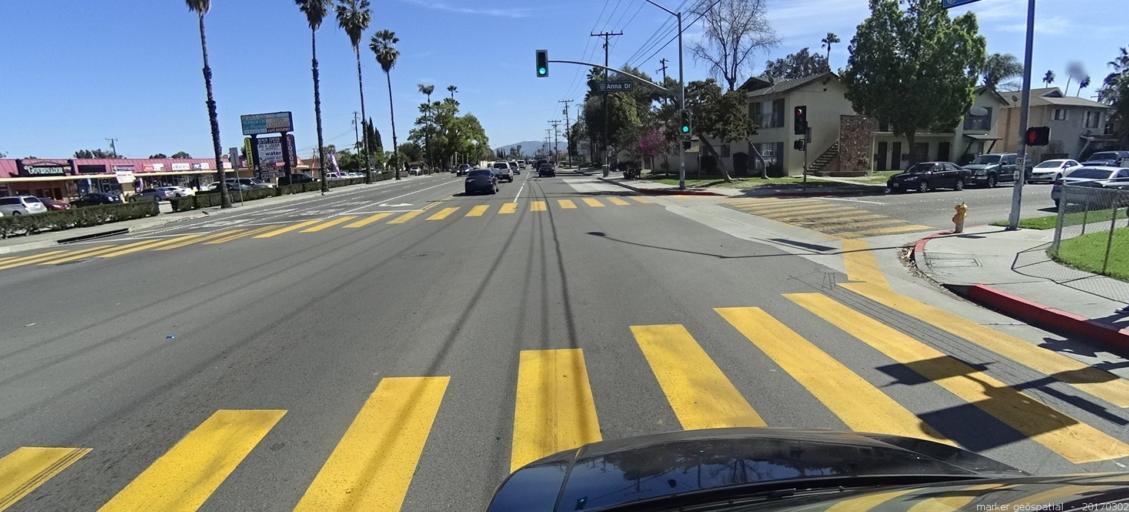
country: US
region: California
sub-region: Orange County
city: Anaheim
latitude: 33.8472
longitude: -117.8980
